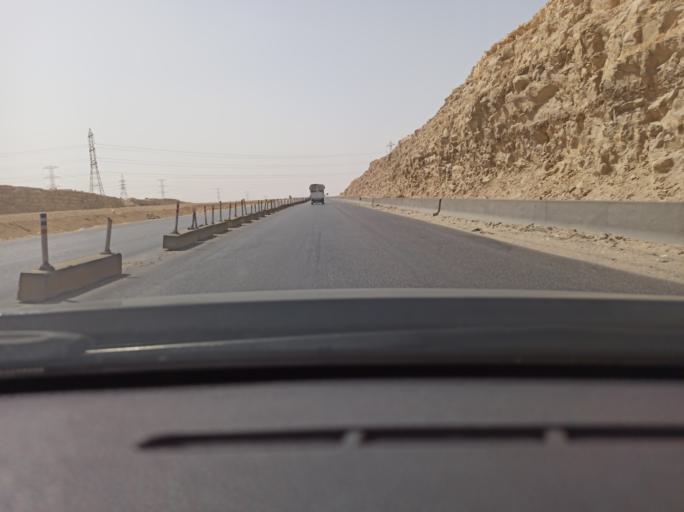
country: EG
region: Muhafazat Bani Suwayf
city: Bush
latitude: 29.1505
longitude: 31.2329
